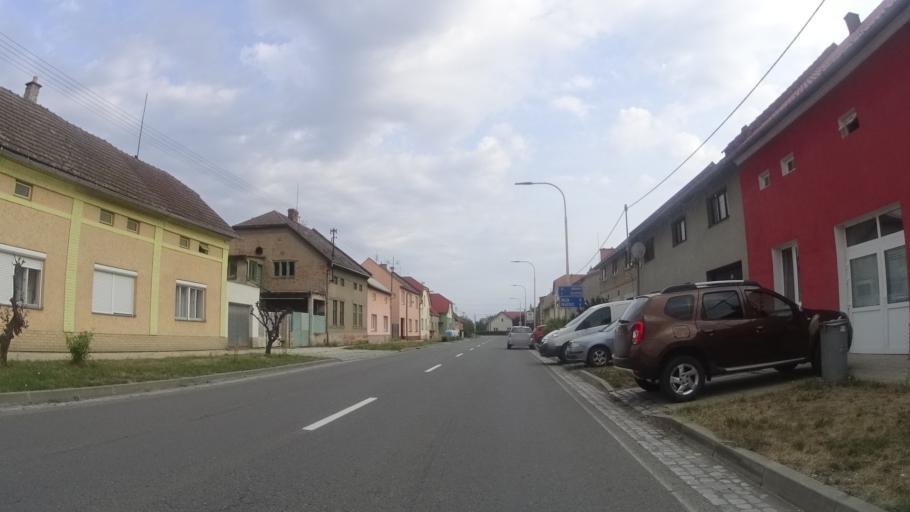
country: CZ
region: Zlin
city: Chropyne
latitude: 49.3540
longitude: 17.3747
